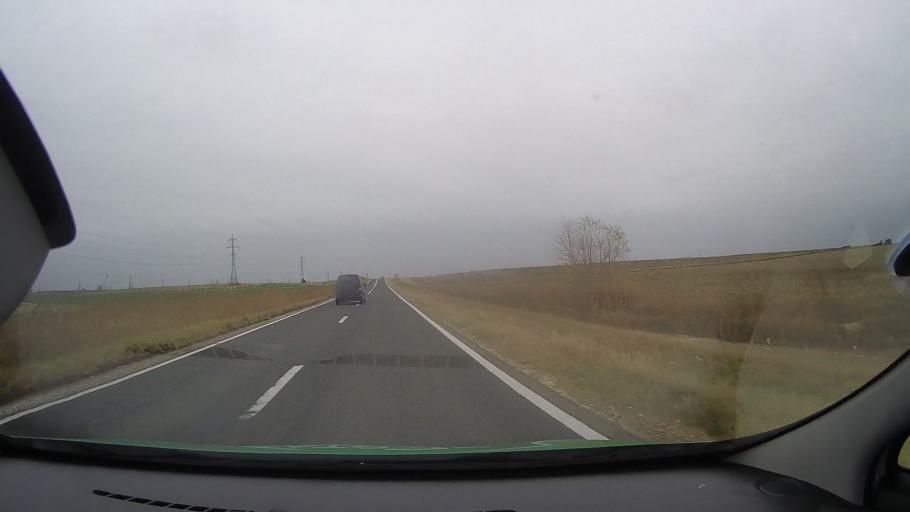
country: RO
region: Constanta
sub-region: Comuna Ciobanu
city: Ciobanu
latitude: 44.6951
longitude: 27.9839
